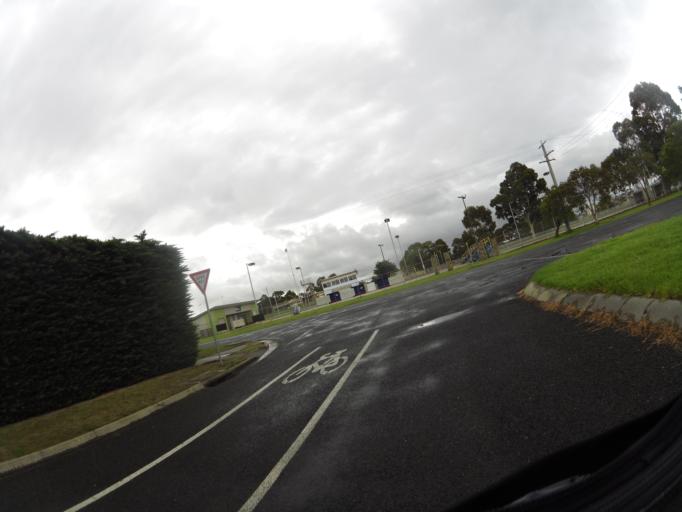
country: AU
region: Victoria
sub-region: East Gippsland
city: Bairnsdale
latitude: -37.8308
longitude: 147.6260
